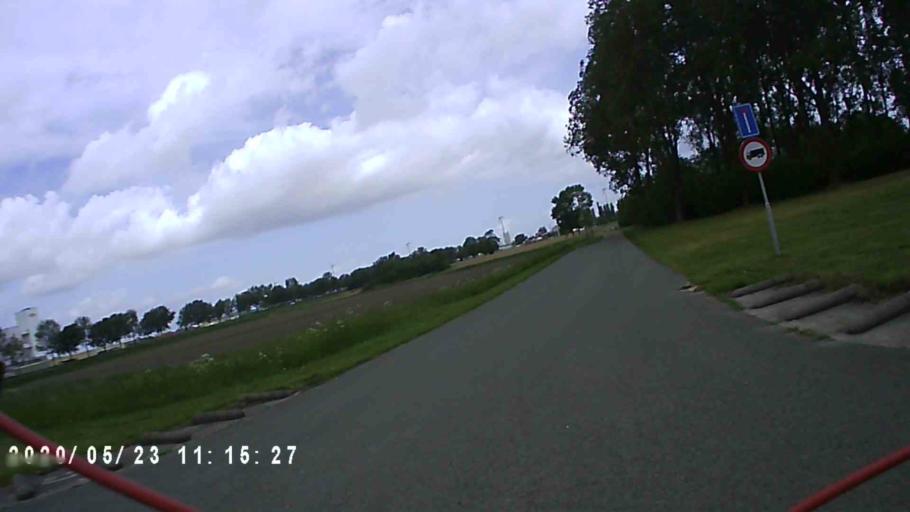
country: NL
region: Groningen
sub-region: Gemeente Delfzijl
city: Delfzijl
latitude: 53.3073
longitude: 6.9645
